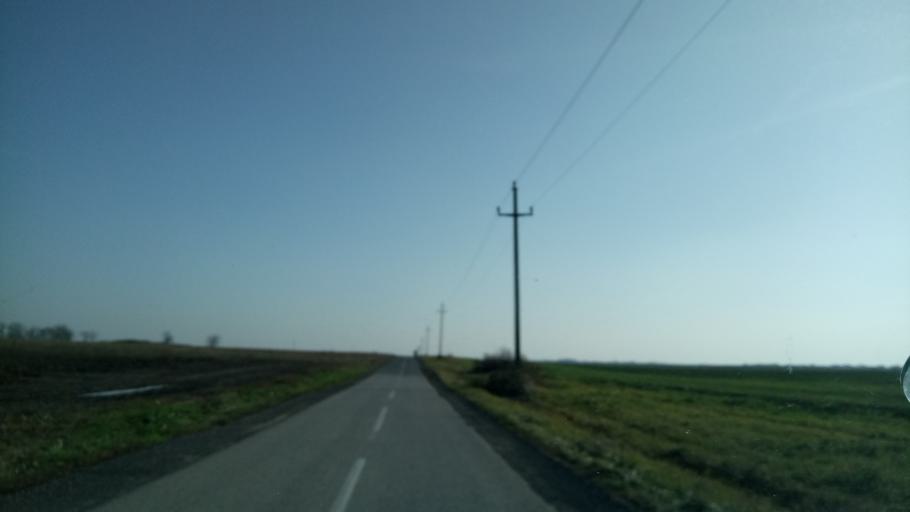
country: RS
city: Ljukovo
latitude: 45.0408
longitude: 20.0373
